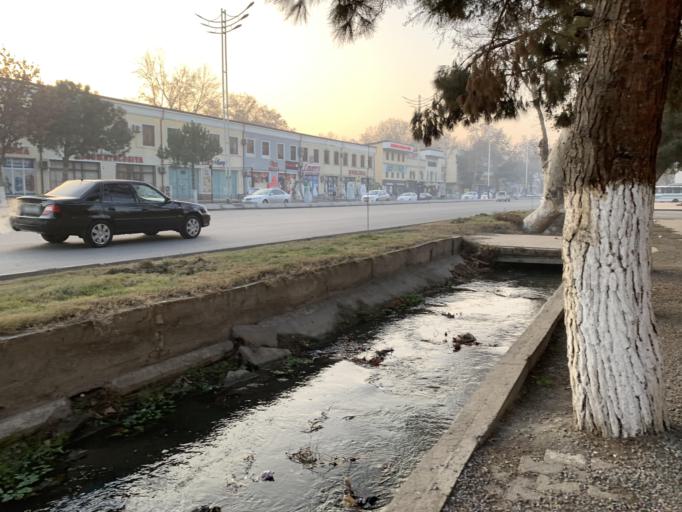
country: UZ
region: Fergana
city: Qo`qon
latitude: 40.5471
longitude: 70.9275
